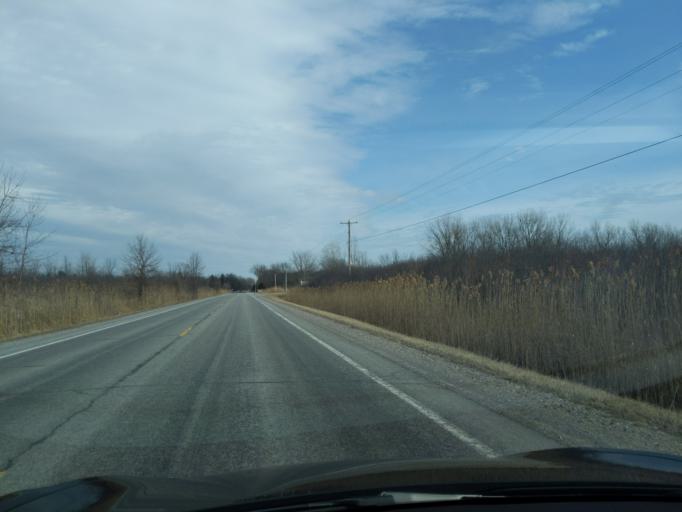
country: US
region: Michigan
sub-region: Bay County
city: Bay City
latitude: 43.6676
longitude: -83.9373
